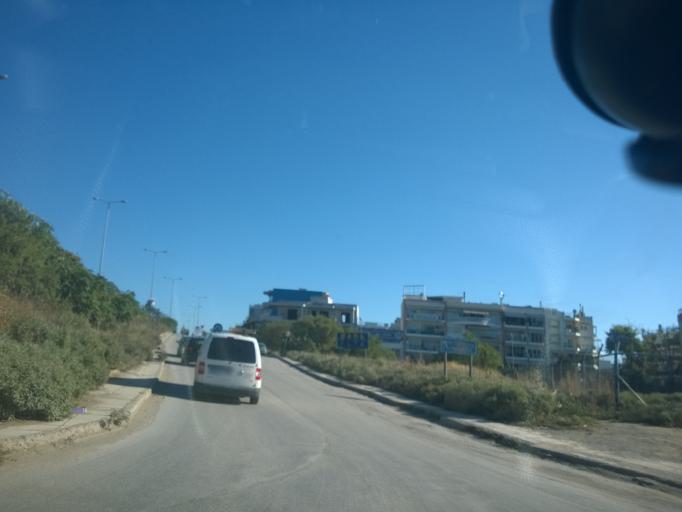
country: GR
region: Central Macedonia
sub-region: Nomos Thessalonikis
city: Kalamaria
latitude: 40.5920
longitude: 22.9654
